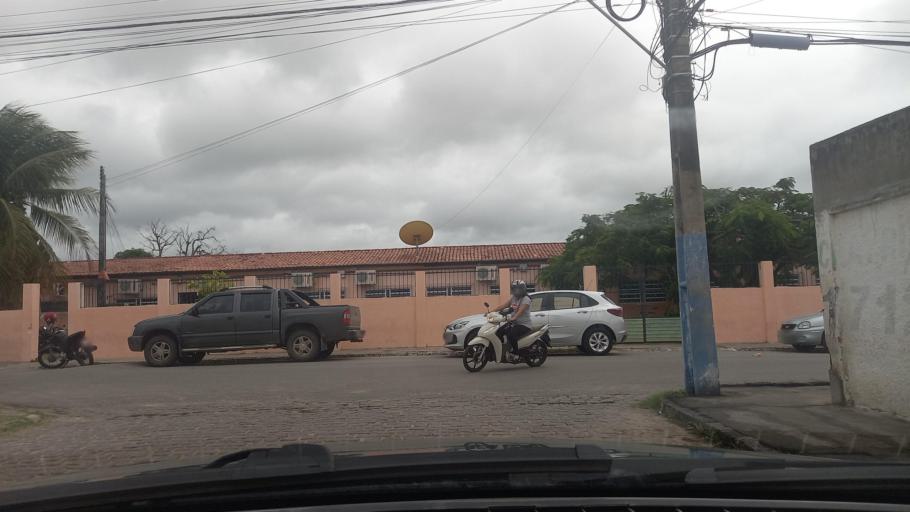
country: BR
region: Alagoas
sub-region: Delmiro Gouveia
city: Delmiro Gouveia
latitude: -9.3890
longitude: -37.9985
